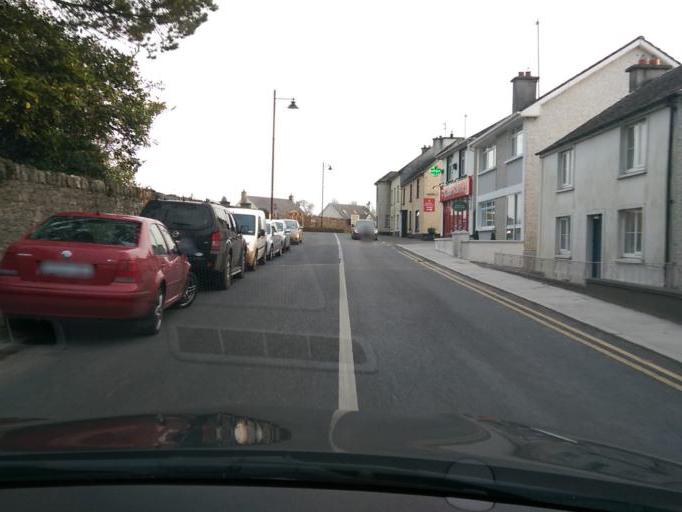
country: IE
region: Leinster
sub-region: An Iarmhi
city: Athlone
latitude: 53.4704
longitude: -7.8639
